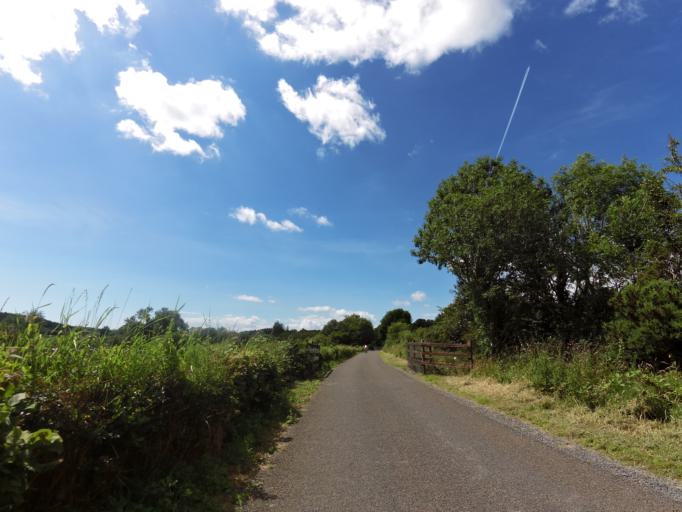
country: IE
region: Munster
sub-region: Waterford
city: Portlaw
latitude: 52.2381
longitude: -7.2920
